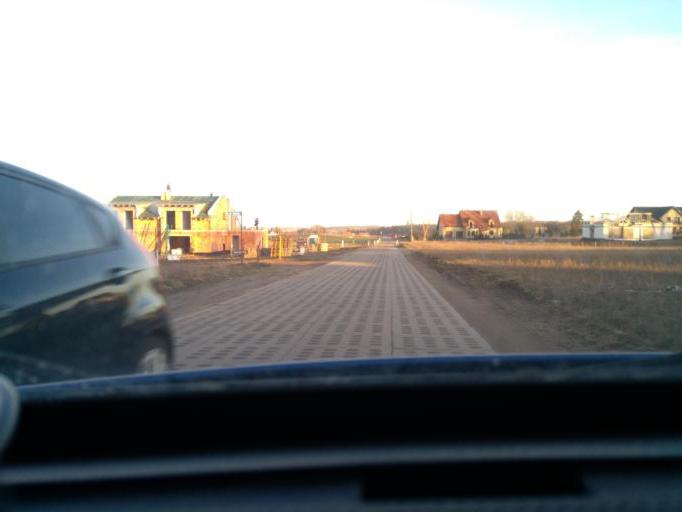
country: PL
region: Pomeranian Voivodeship
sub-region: Powiat kartuski
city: Banino
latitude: 54.3823
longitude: 18.3959
